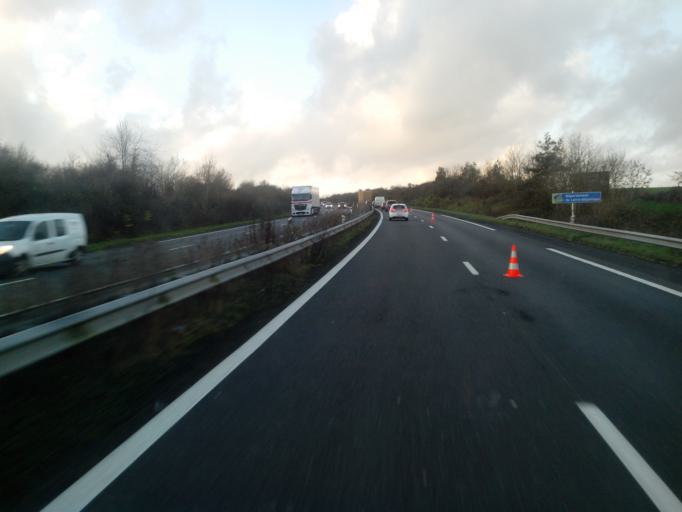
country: FR
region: Pays de la Loire
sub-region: Departement de Maine-et-Loire
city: Tillieres
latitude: 47.1525
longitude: -1.1989
